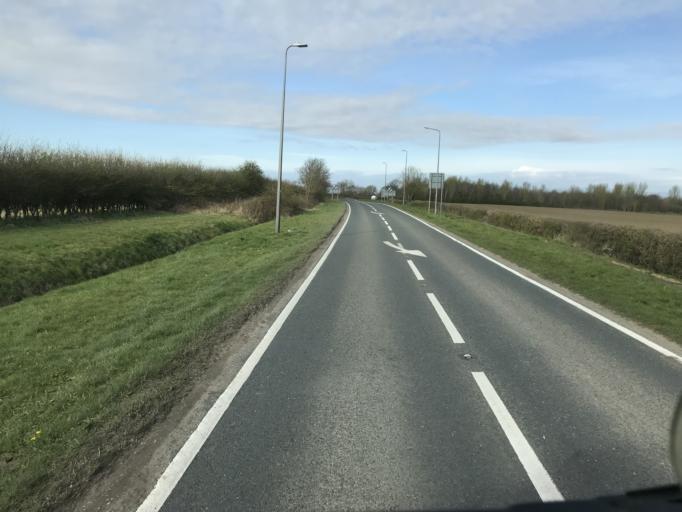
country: GB
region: England
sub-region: Lincolnshire
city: Market Rasen
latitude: 53.3860
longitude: -0.3767
